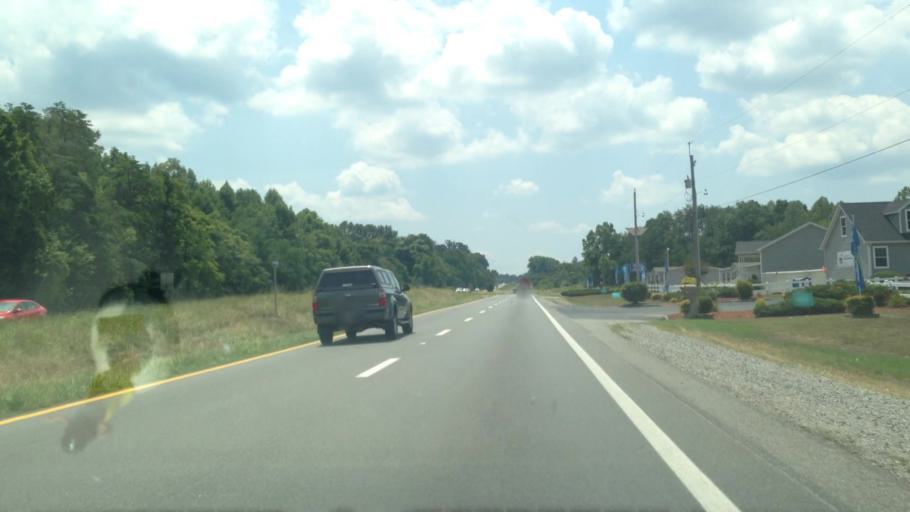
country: US
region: Virginia
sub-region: Henry County
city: Chatmoss
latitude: 36.5981
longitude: -79.8625
